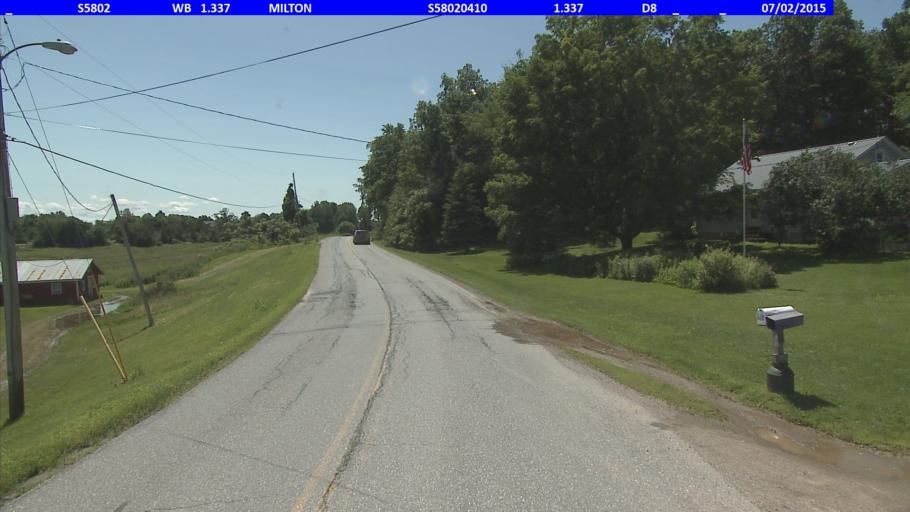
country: US
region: Vermont
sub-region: Chittenden County
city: Milton
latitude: 44.6261
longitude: -73.1977
